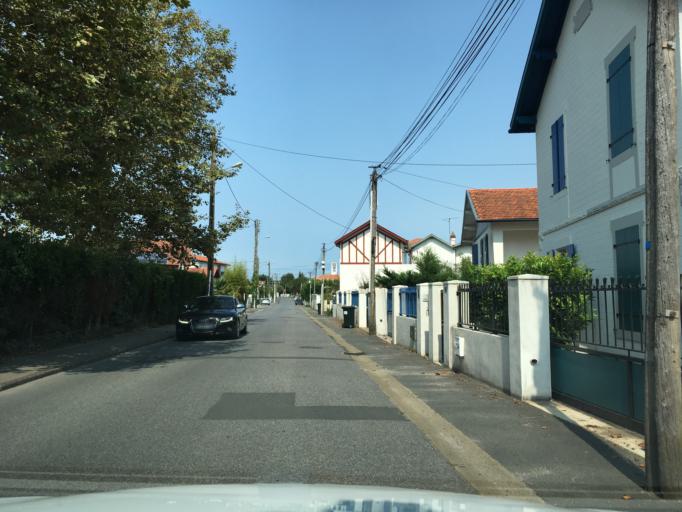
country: FR
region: Aquitaine
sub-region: Departement des Pyrenees-Atlantiques
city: Biarritz
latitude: 43.4829
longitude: -1.5352
